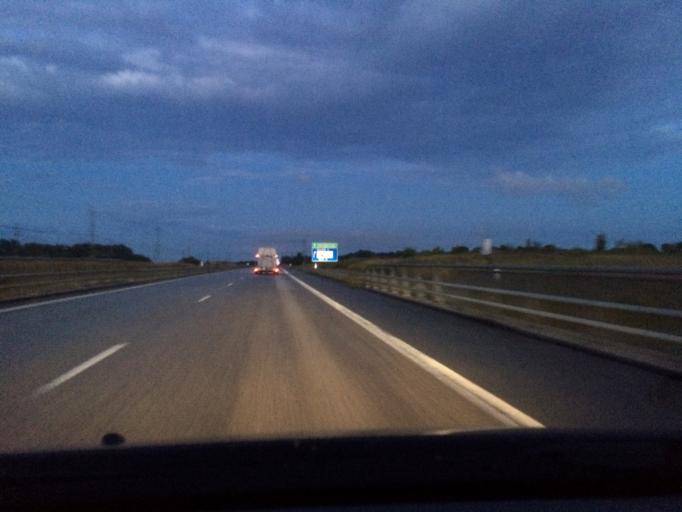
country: SE
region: Skane
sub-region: Malmo
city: Bunkeflostrand
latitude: 55.5569
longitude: 12.9417
